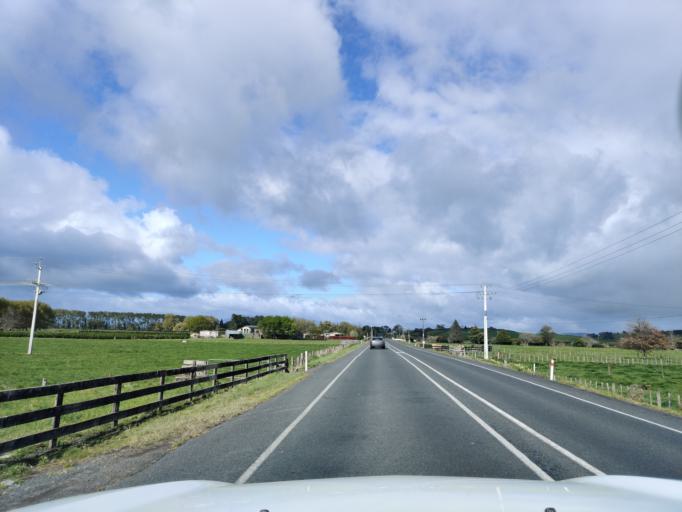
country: NZ
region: Waikato
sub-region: Hamilton City
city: Hamilton
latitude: -37.8075
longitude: 175.2394
